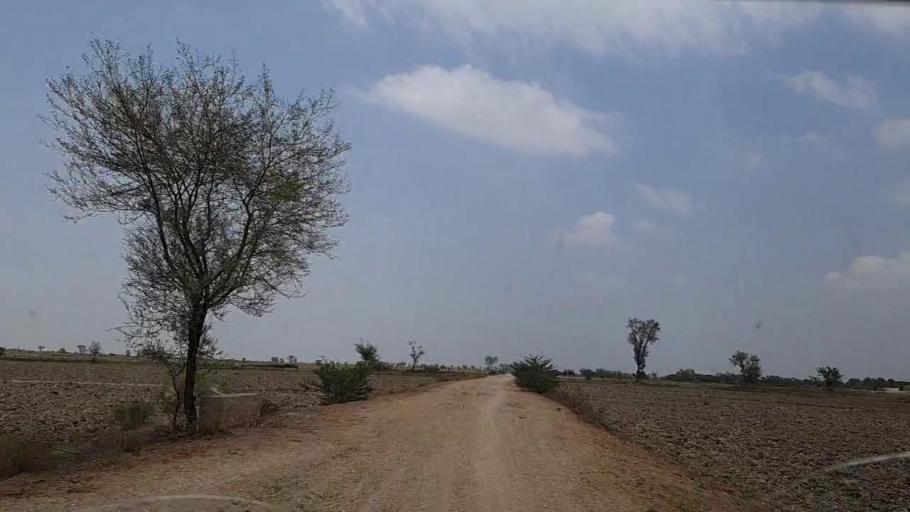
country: PK
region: Sindh
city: Phulji
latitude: 26.8247
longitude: 67.6405
